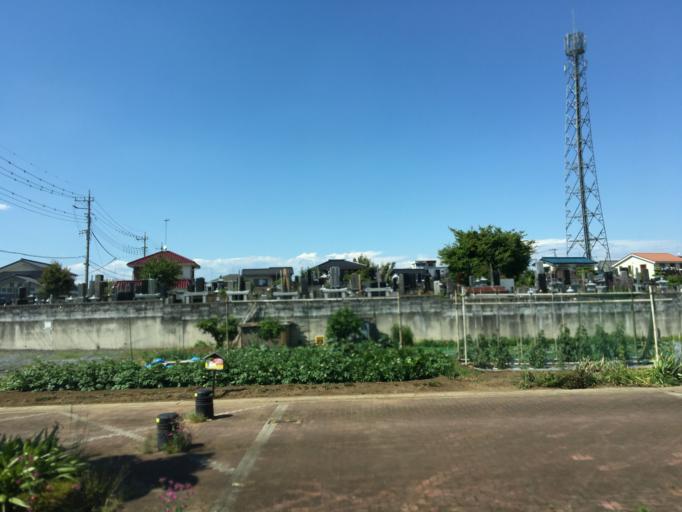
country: JP
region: Saitama
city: Sakado
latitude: 36.0028
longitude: 139.3900
